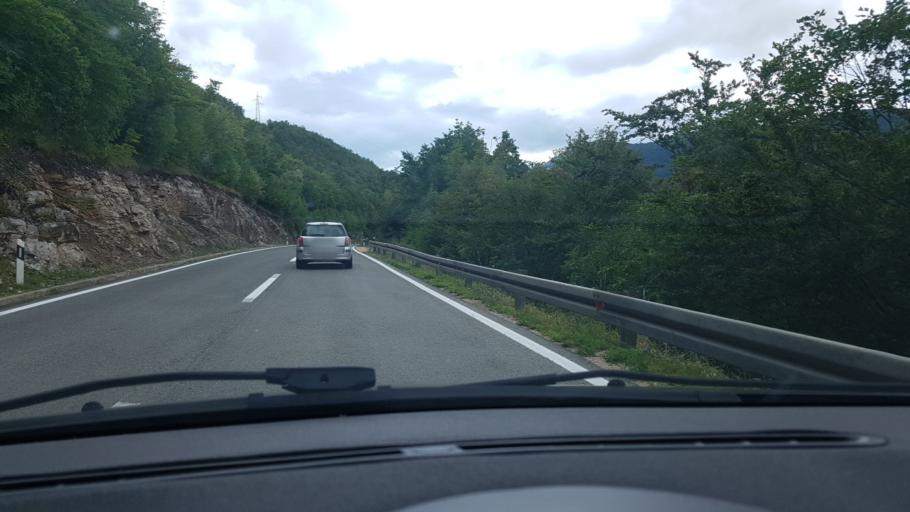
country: HR
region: Zadarska
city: Gracac
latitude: 44.2763
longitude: 15.8190
